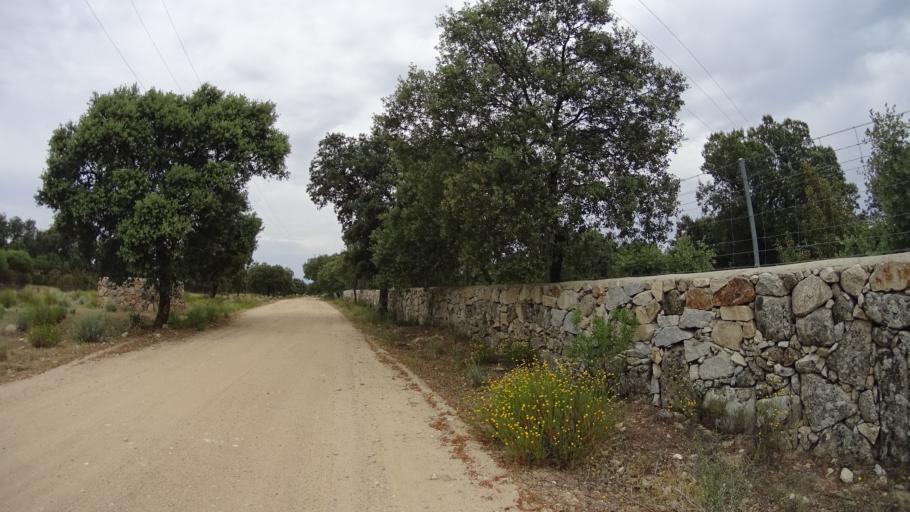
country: ES
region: Madrid
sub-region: Provincia de Madrid
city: Colmenarejo
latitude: 40.5475
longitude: -4.0385
